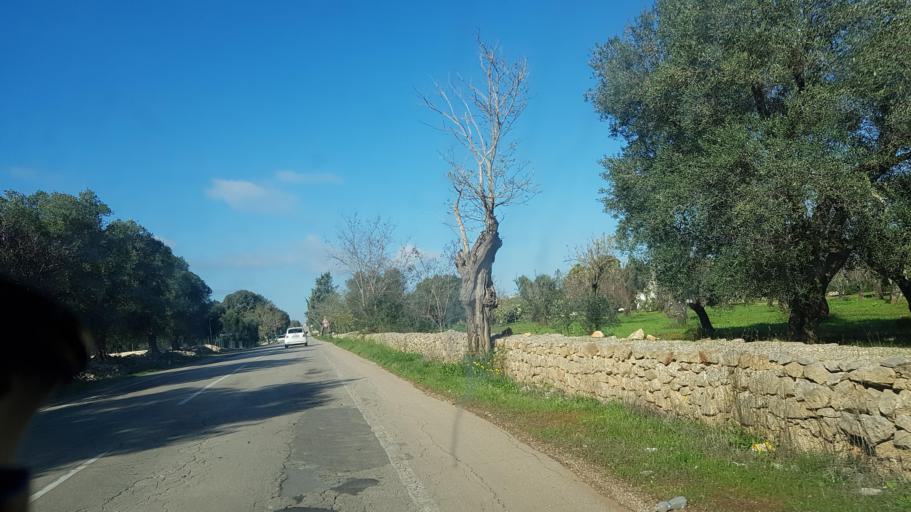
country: IT
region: Apulia
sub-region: Provincia di Brindisi
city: Carovigno
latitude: 40.6818
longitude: 17.6825
